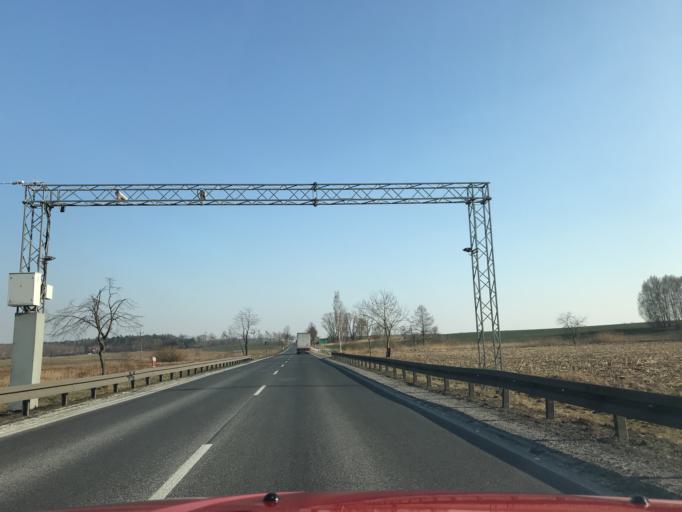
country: PL
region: Greater Poland Voivodeship
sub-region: Powiat sredzki
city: Nowe Miasto nad Warta
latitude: 52.0830
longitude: 17.4039
